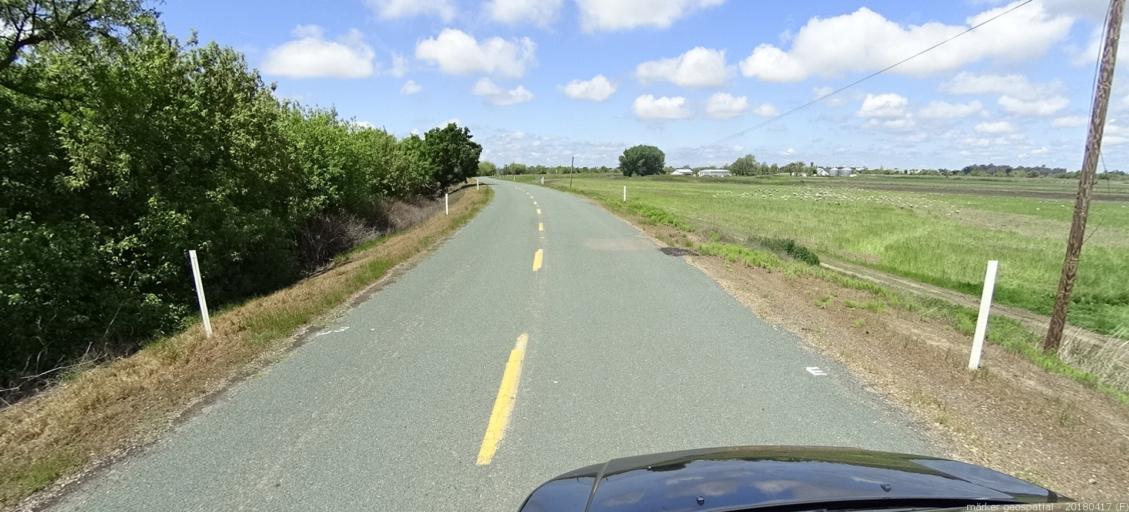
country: US
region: California
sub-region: Solano County
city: Rio Vista
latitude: 38.1507
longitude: -121.5873
